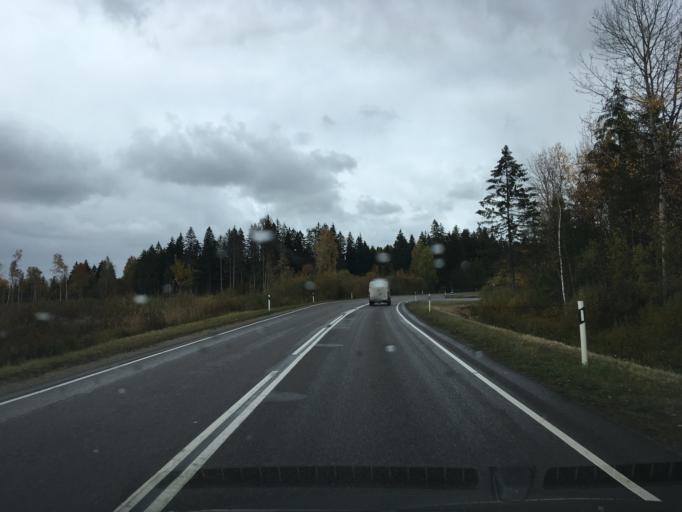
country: EE
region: Harju
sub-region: Anija vald
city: Kehra
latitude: 59.3397
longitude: 25.3098
